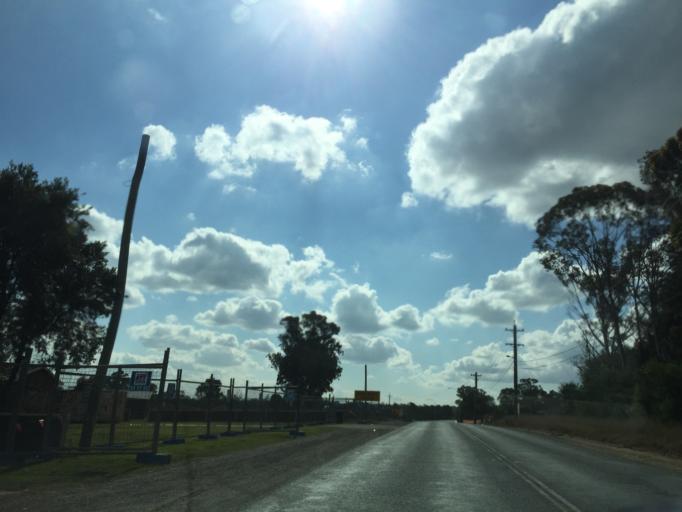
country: AU
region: New South Wales
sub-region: Blacktown
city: Rouse Hill
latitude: -33.7000
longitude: 150.8950
